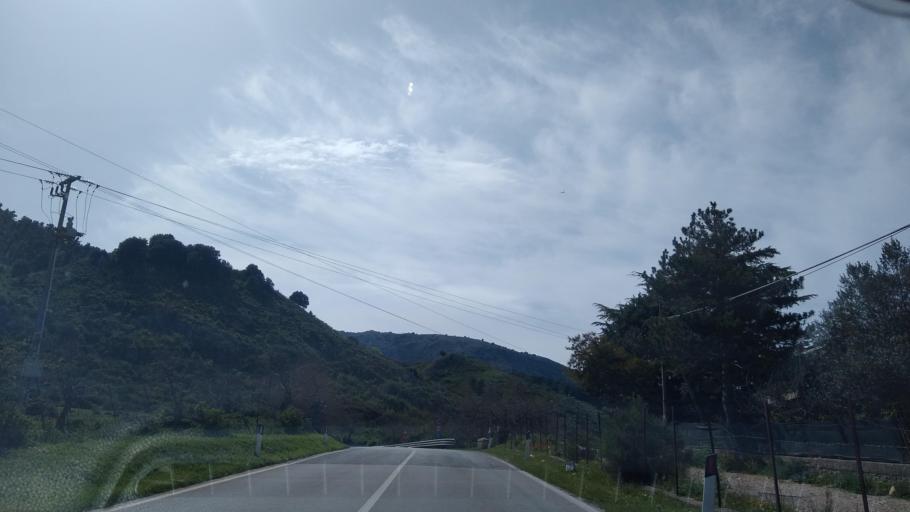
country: IT
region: Sicily
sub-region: Palermo
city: Pioppo
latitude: 38.0374
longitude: 13.2095
